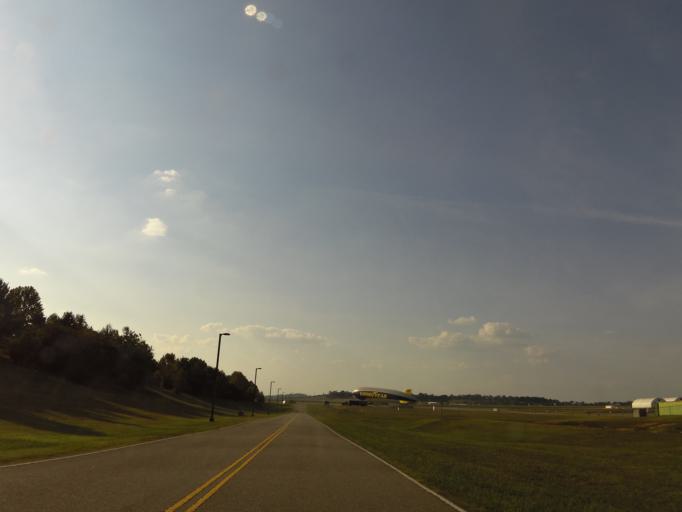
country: US
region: Tennessee
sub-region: Blount County
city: Alcoa
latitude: 35.7971
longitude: -83.9957
